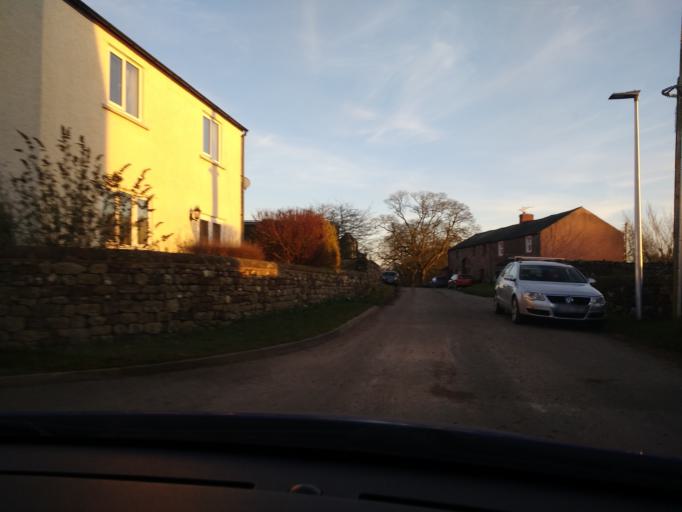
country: GB
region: England
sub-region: Cumbria
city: Appleby-in-Westmorland
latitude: 54.6185
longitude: -2.4769
